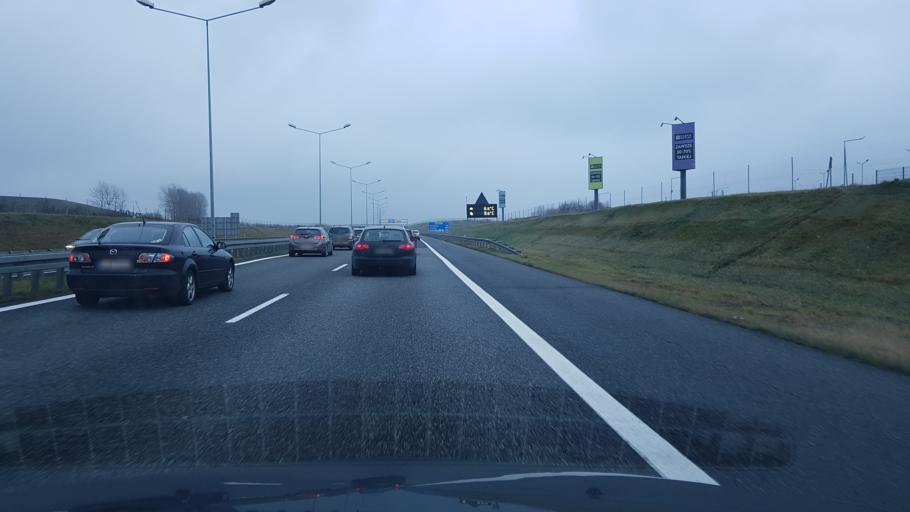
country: PL
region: Silesian Voivodeship
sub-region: Powiat gliwicki
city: Knurow
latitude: 50.2597
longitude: 18.6586
